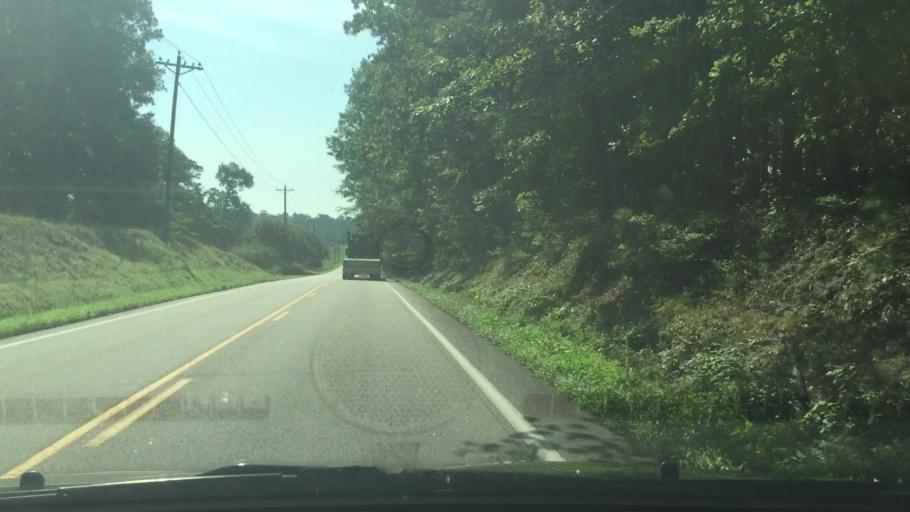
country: US
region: Virginia
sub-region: Sussex County
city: Sussex
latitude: 37.0547
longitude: -77.3238
